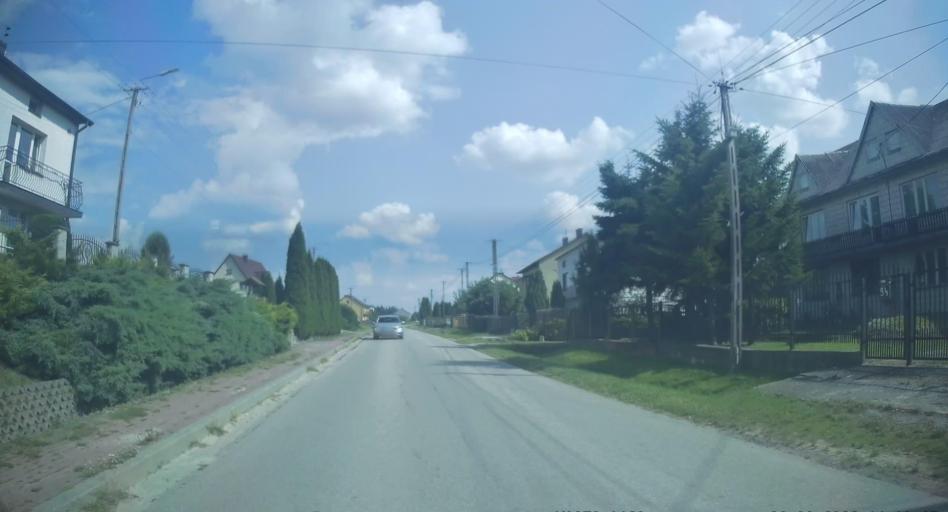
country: PL
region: Swietokrzyskie
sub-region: Powiat kielecki
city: Checiny
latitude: 50.8164
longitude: 20.4022
